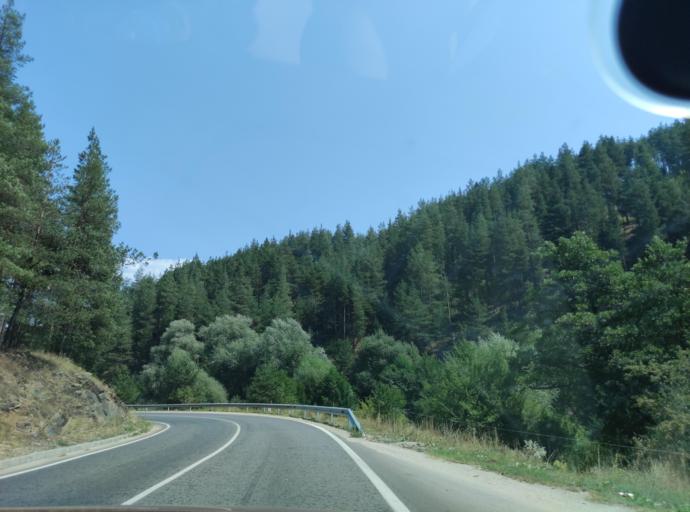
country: BG
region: Blagoevgrad
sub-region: Obshtina Razlog
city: Razlog
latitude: 41.8915
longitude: 23.5349
